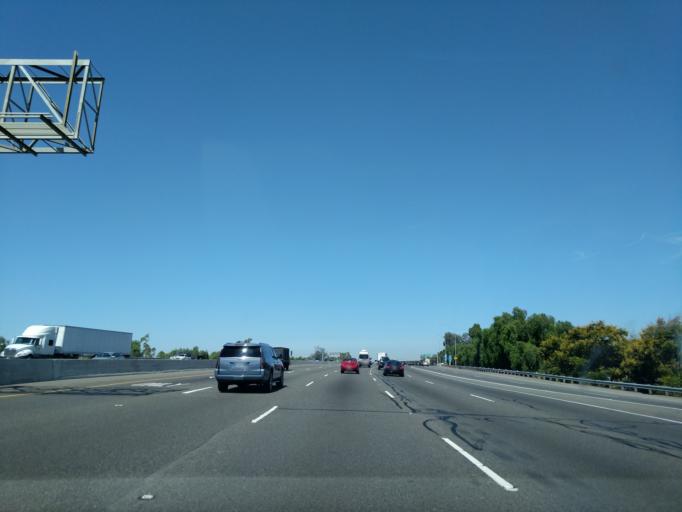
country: US
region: California
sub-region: Orange County
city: Laguna Woods
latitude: 33.6704
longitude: -117.7546
